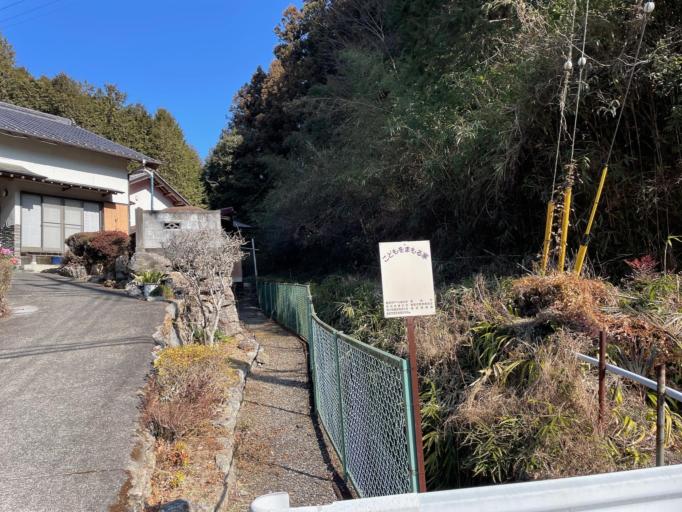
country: JP
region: Saitama
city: Hanno
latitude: 35.8517
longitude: 139.2528
